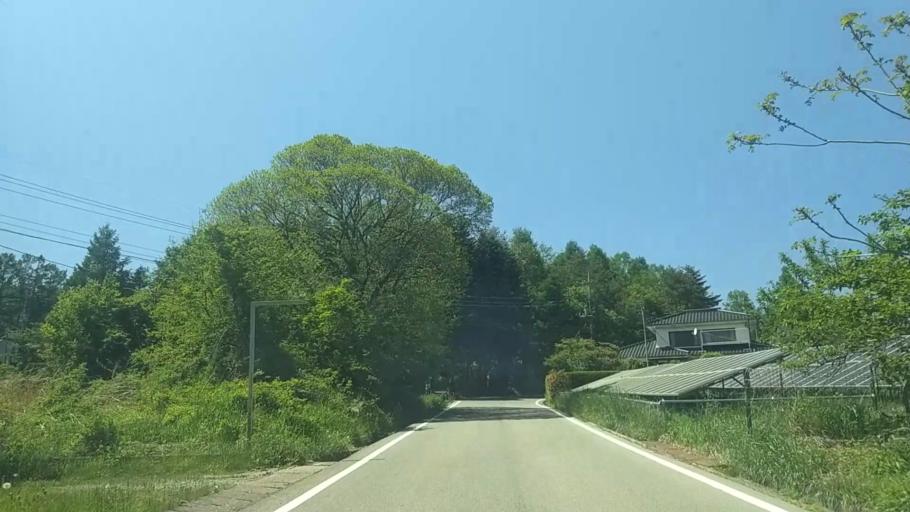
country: JP
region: Yamanashi
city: Nirasaki
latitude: 35.9019
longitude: 138.4477
